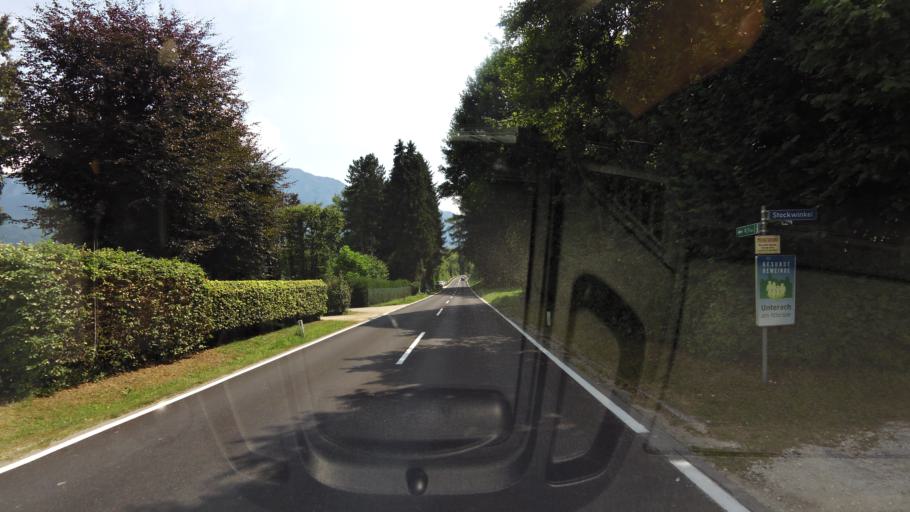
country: AT
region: Upper Austria
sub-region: Politischer Bezirk Vocklabruck
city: Steinbach am Attersee
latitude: 47.8397
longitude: 13.5226
